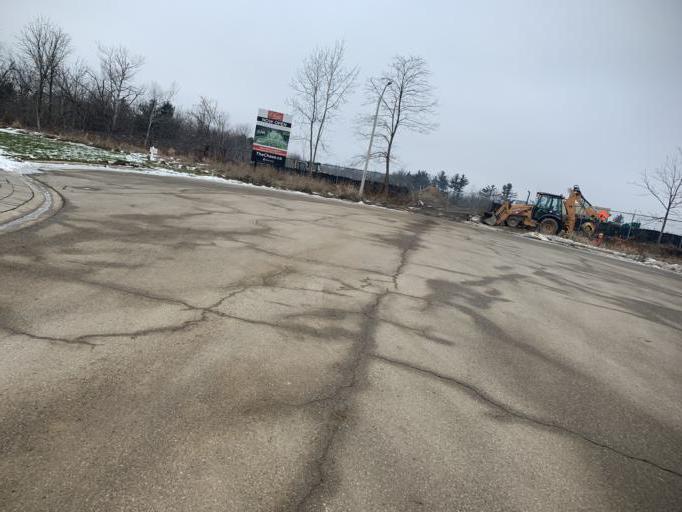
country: CA
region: Ontario
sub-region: Halton
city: Milton
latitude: 43.6606
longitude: -79.9248
